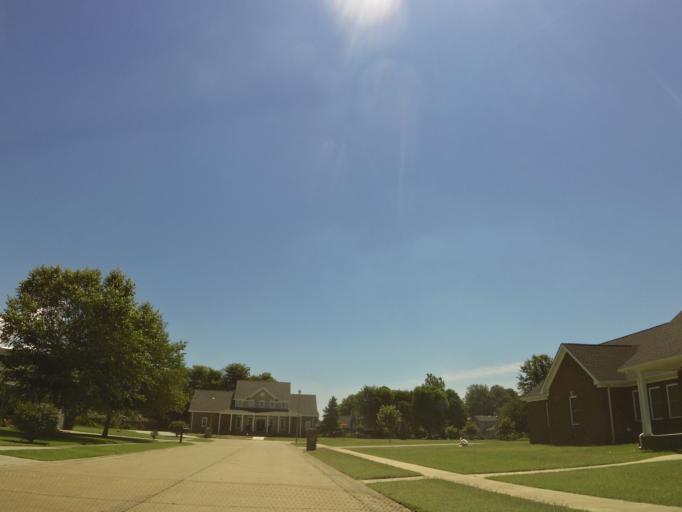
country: US
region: Missouri
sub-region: New Madrid County
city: New Madrid
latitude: 36.5995
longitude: -89.5252
